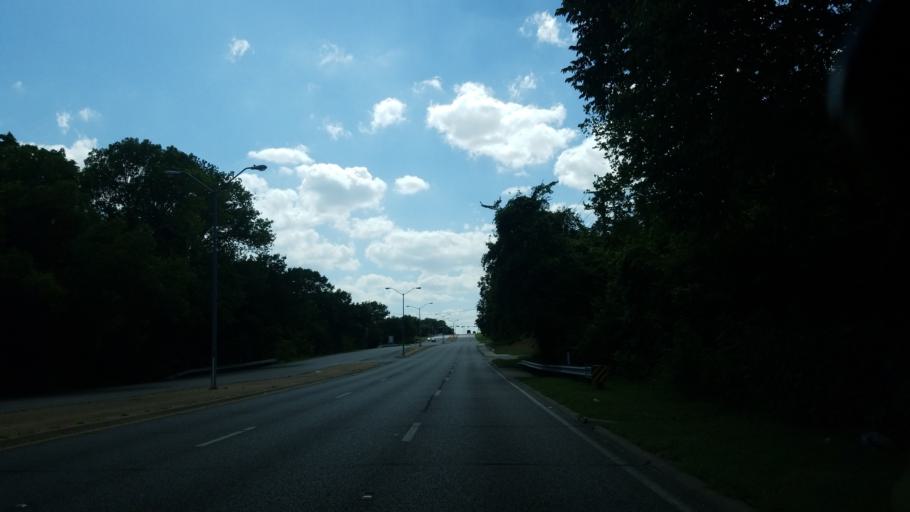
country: US
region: Texas
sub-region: Dallas County
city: Balch Springs
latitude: 32.7635
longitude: -96.6950
